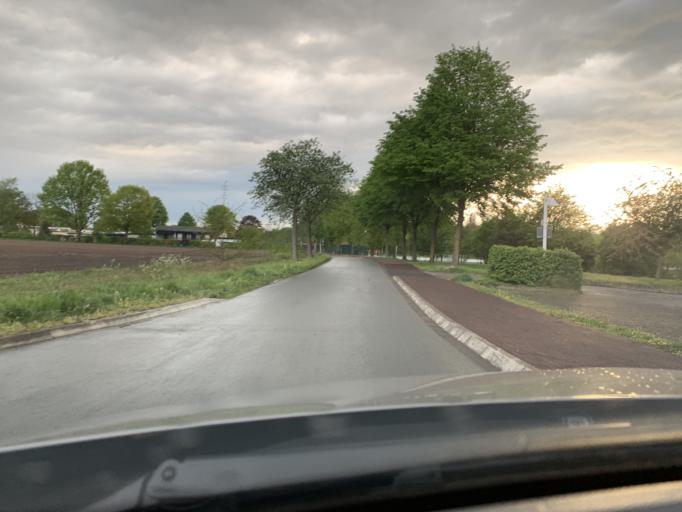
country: DE
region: North Rhine-Westphalia
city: Rietberg
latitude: 51.7995
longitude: 8.3726
